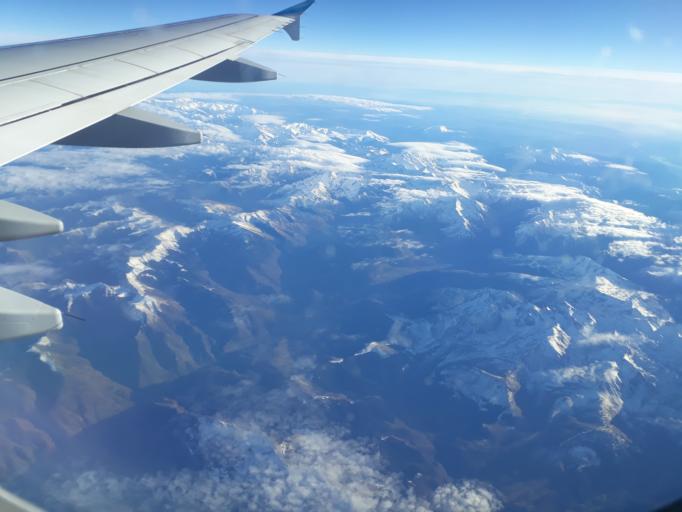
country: FR
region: Midi-Pyrenees
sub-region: Departement des Hautes-Pyrenees
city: Gerde
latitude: 43.0562
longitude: 0.2376
